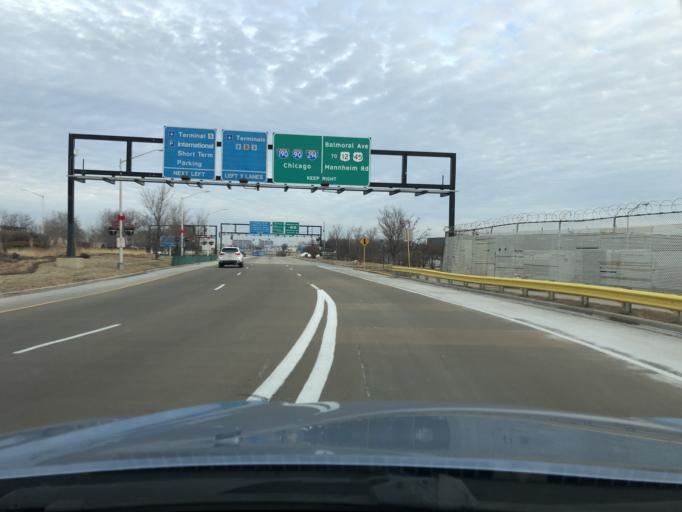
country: US
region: Illinois
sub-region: Cook County
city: Rosemont
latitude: 41.9748
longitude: -87.8861
